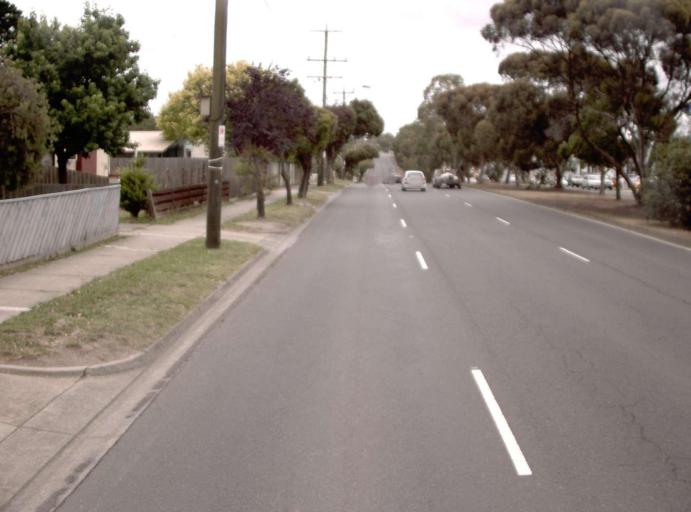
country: AU
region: Victoria
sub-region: Maroondah
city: Ringwood East
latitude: -37.7989
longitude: 145.2529
